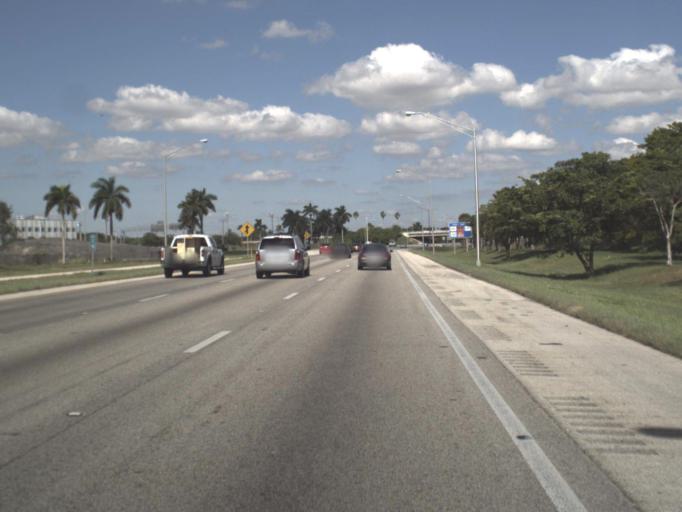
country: US
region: Florida
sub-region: Miami-Dade County
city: The Crossings
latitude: 25.6668
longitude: -80.3871
